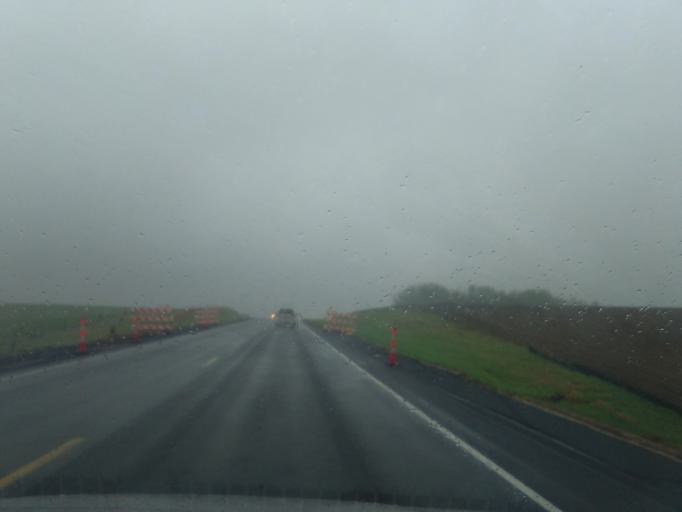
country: US
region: Nebraska
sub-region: Wayne County
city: Wayne
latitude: 42.1877
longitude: -97.1771
